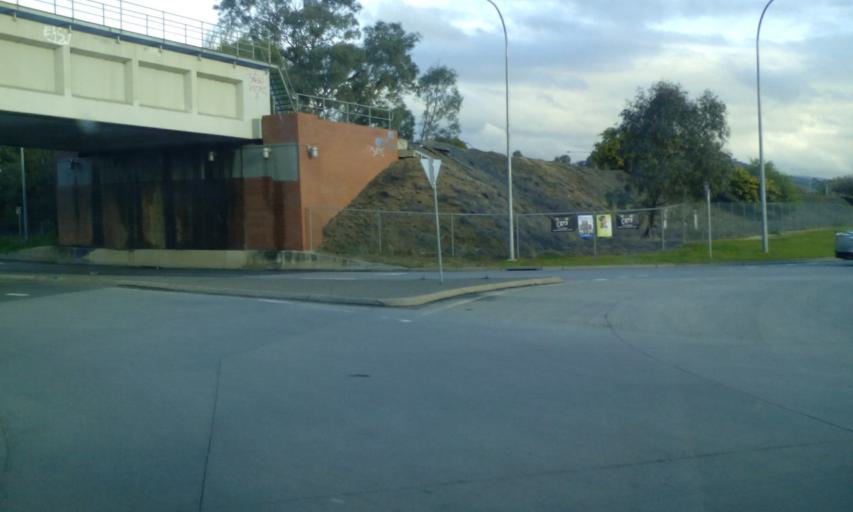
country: AU
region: New South Wales
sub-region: Albury Municipality
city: East Albury
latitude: -36.0906
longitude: 146.9230
